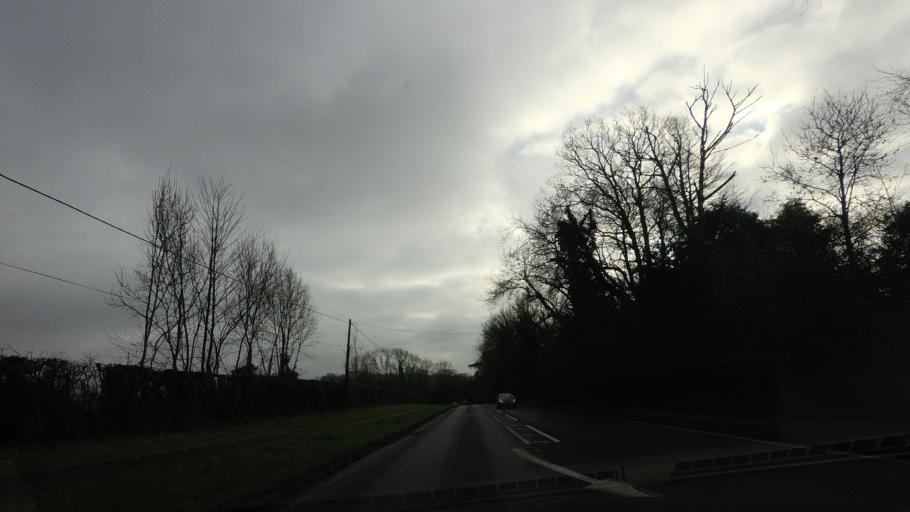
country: GB
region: England
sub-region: East Sussex
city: Robertsbridge
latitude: 51.0441
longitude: 0.4470
